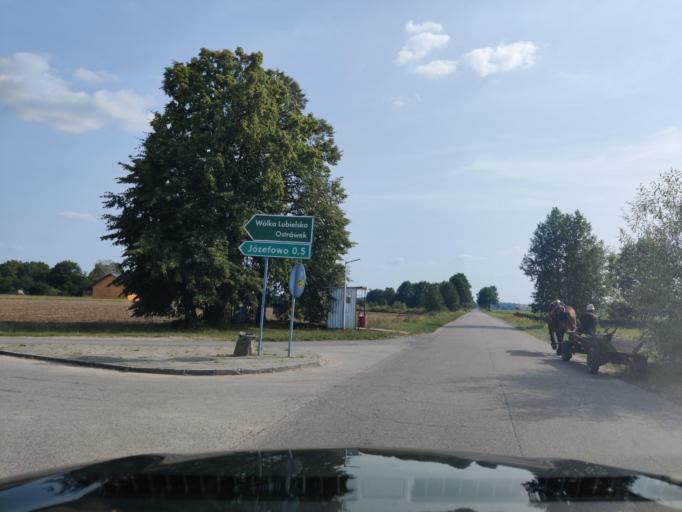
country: PL
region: Masovian Voivodeship
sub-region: Powiat wyszkowski
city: Rzasnik
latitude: 52.7527
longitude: 21.3535
